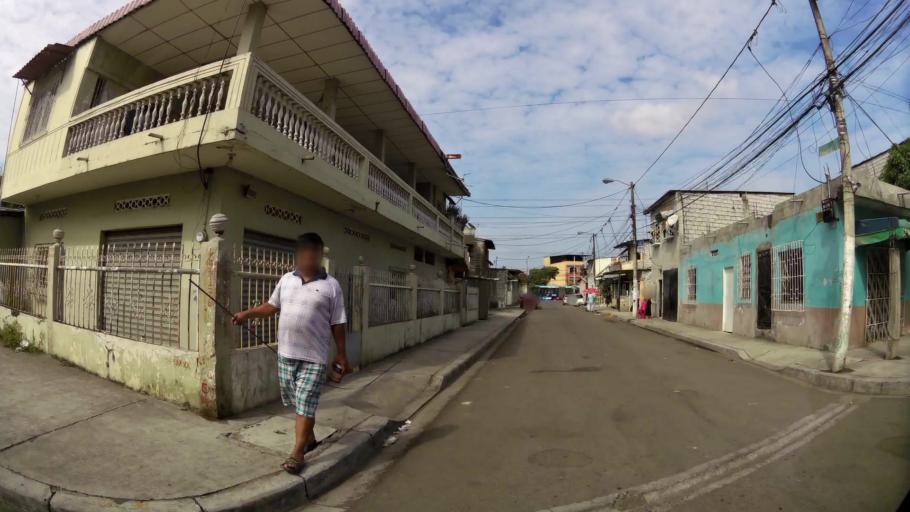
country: EC
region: Guayas
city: Guayaquil
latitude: -2.2591
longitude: -79.8833
